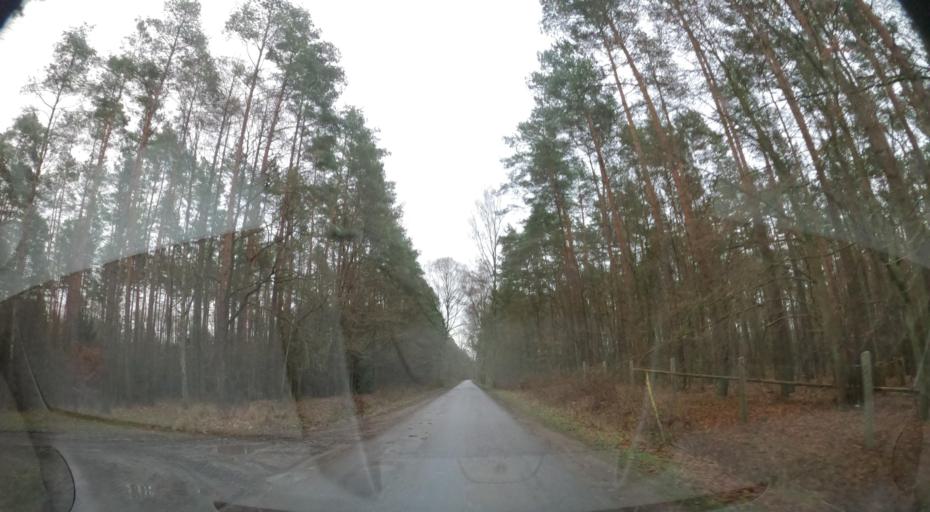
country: PL
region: Greater Poland Voivodeship
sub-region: Powiat zlotowski
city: Krajenka
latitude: 53.2863
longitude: 17.0658
